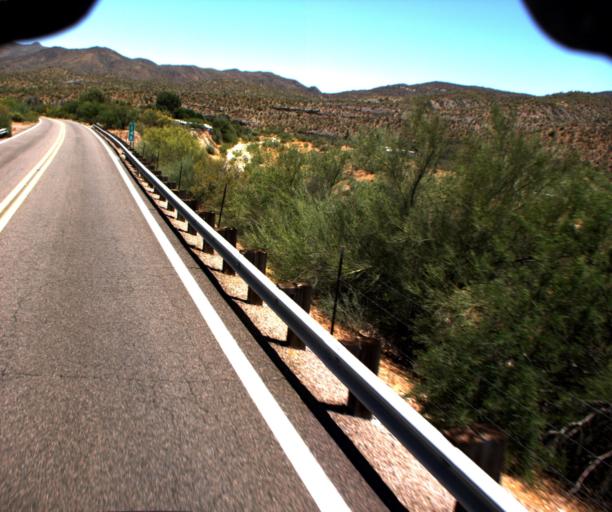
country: US
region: Arizona
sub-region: Pinal County
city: Kearny
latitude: 33.0966
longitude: -110.7311
